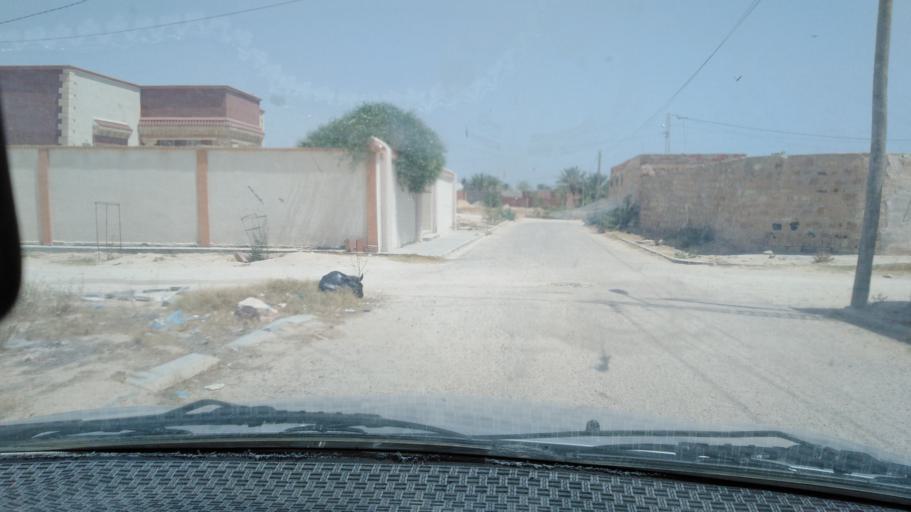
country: TN
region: Qabis
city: Gabes
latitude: 33.9569
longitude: 9.9935
